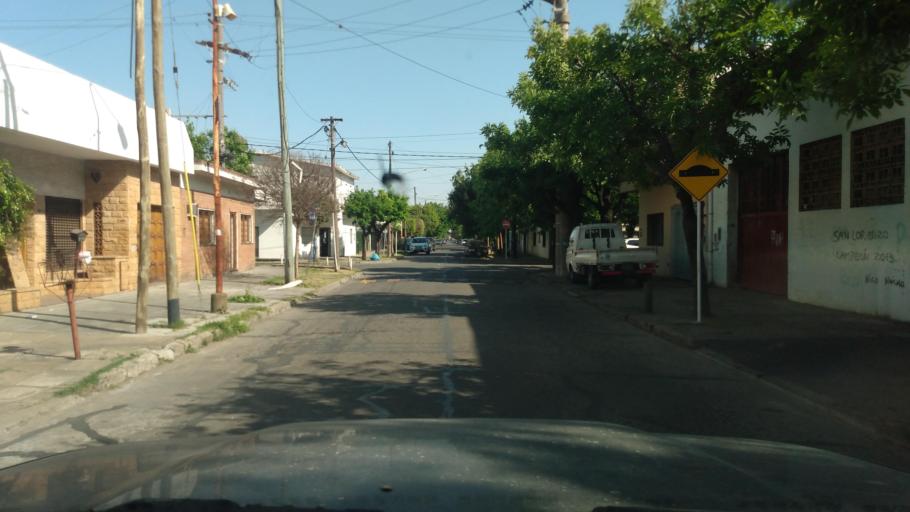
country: AR
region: Buenos Aires
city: San Justo
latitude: -34.6700
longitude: -58.5769
